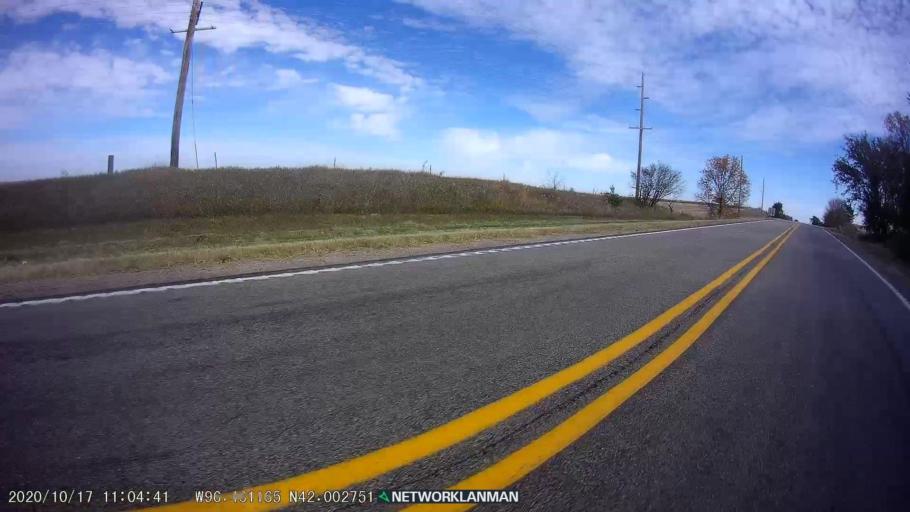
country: US
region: Nebraska
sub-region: Thurston County
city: Macy
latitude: 42.0027
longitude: -96.4612
